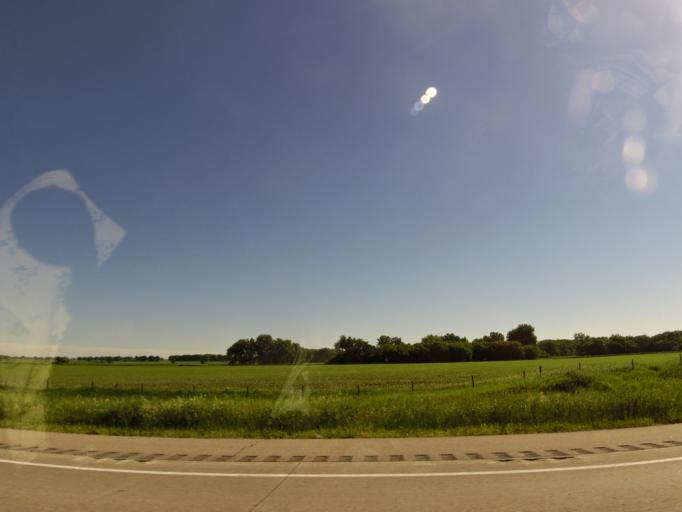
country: US
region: Minnesota
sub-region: Clay County
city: Barnesville
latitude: 46.6886
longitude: -96.4462
